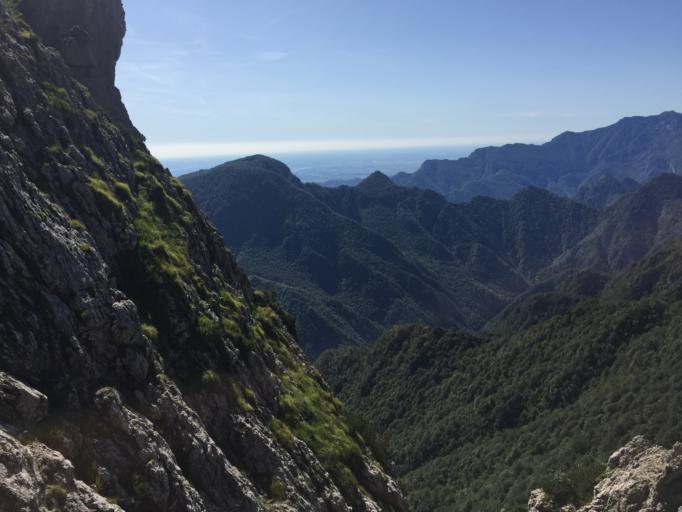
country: IT
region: Friuli Venezia Giulia
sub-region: Provincia di Pordenone
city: Tramonti di Sopra
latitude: 46.3201
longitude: 12.7295
